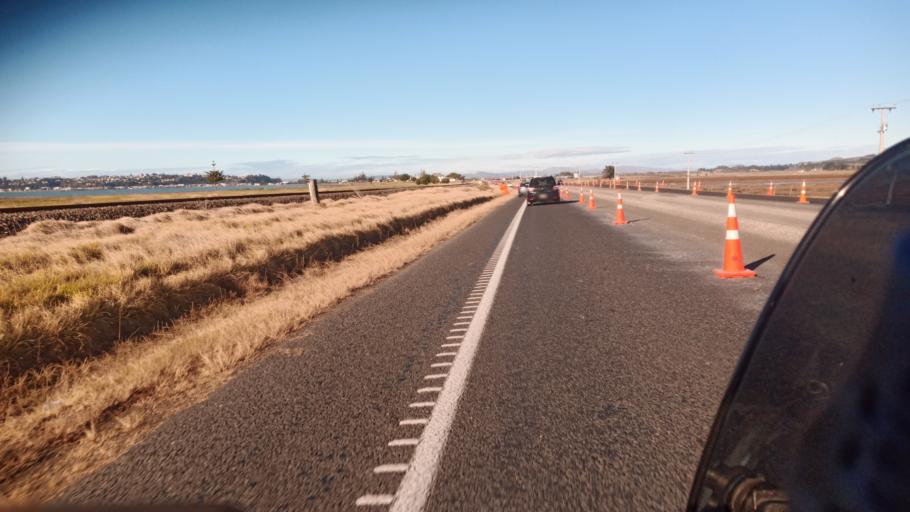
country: NZ
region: Hawke's Bay
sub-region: Napier City
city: Napier
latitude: -39.4529
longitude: 176.8716
